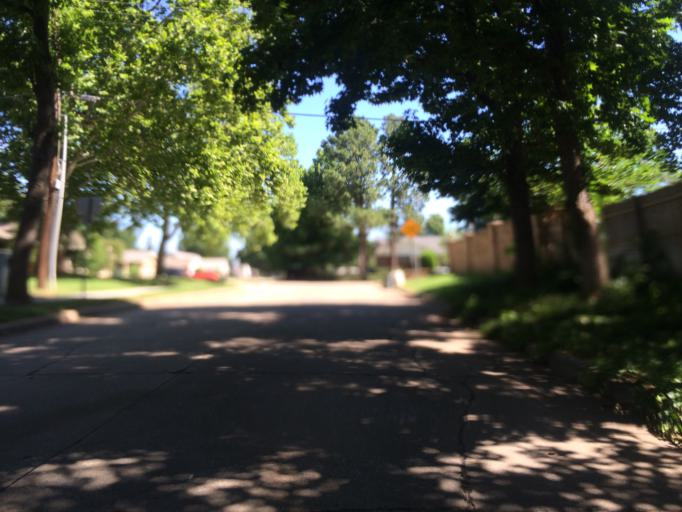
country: US
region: Oklahoma
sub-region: Cleveland County
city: Norman
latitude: 35.2215
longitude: -97.4671
